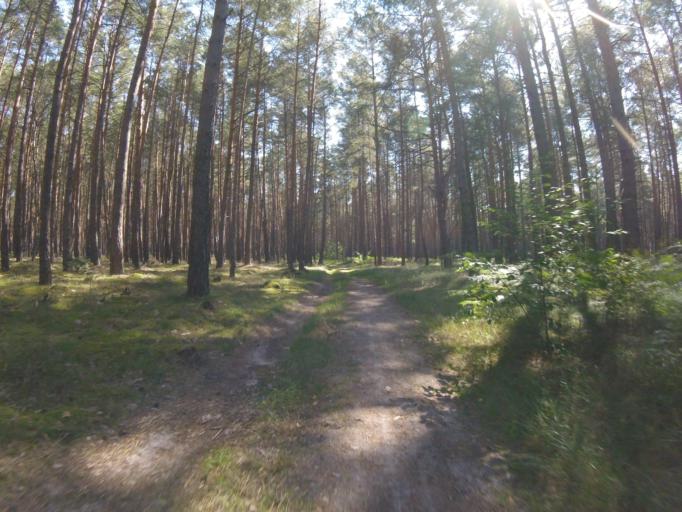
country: DE
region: Brandenburg
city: Bestensee
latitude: 52.2709
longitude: 13.6772
